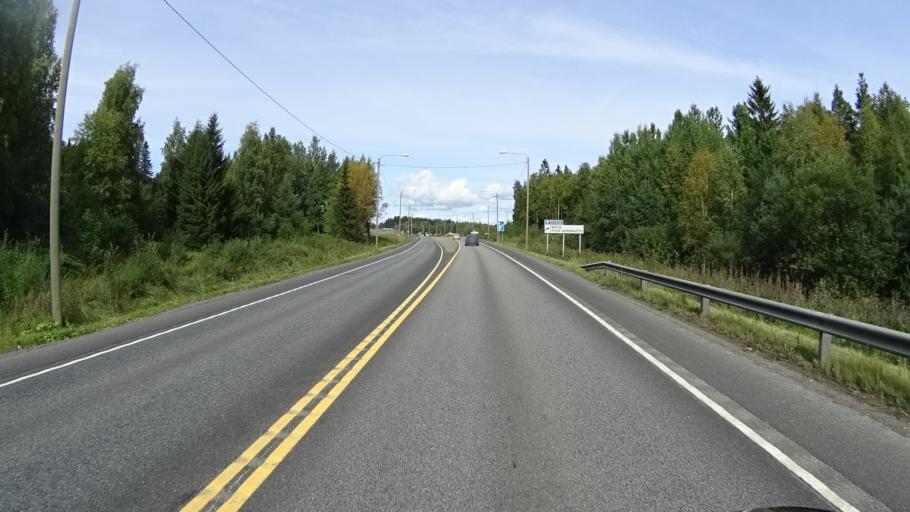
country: FI
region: Pirkanmaa
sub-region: Tampere
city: Haemeenkyroe
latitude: 61.6802
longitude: 23.1618
